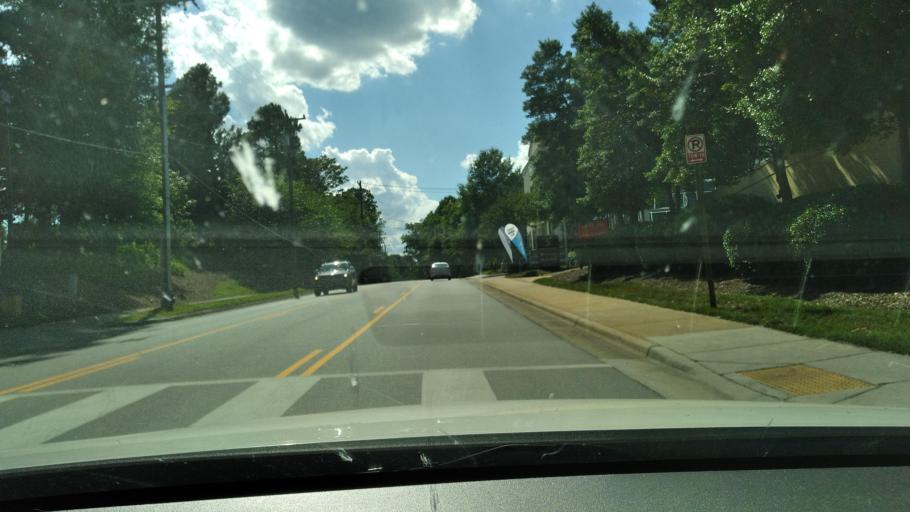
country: US
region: North Carolina
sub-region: Guilford County
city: Greensboro
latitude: 36.0879
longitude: -79.8341
